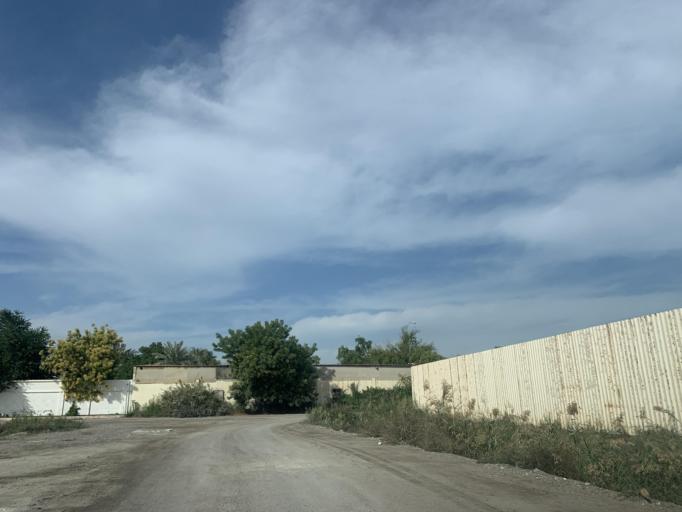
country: BH
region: Central Governorate
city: Madinat Hamad
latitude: 26.1197
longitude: 50.4696
